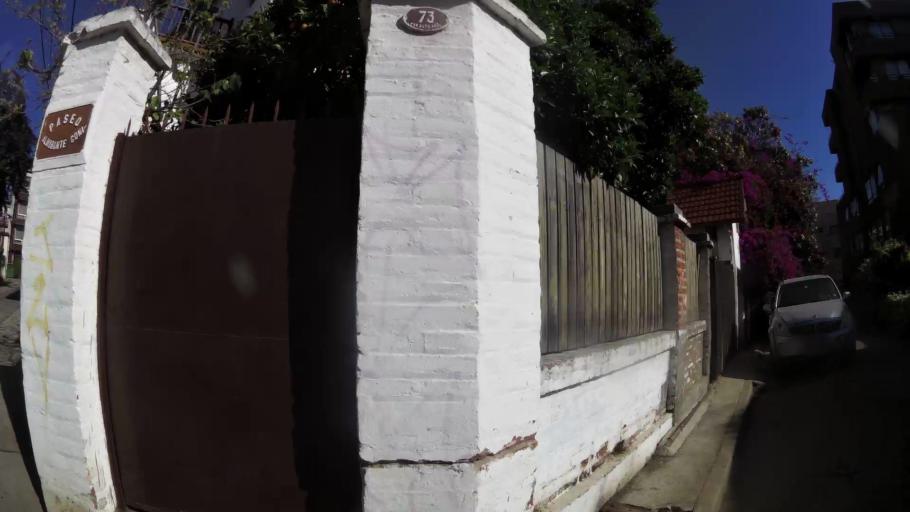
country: CL
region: Valparaiso
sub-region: Provincia de Valparaiso
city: Vina del Mar
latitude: -33.0278
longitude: -71.5581
